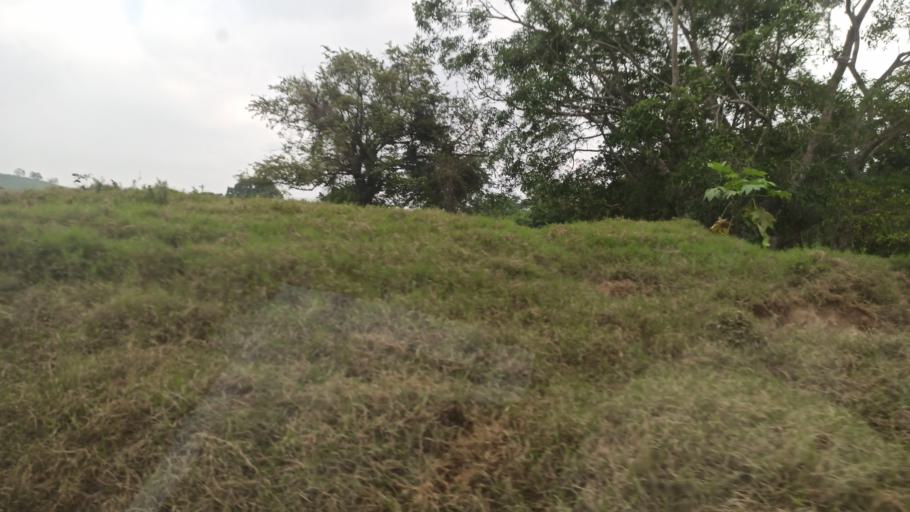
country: MX
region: Puebla
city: San Jose Acateno
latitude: 20.2303
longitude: -97.1322
